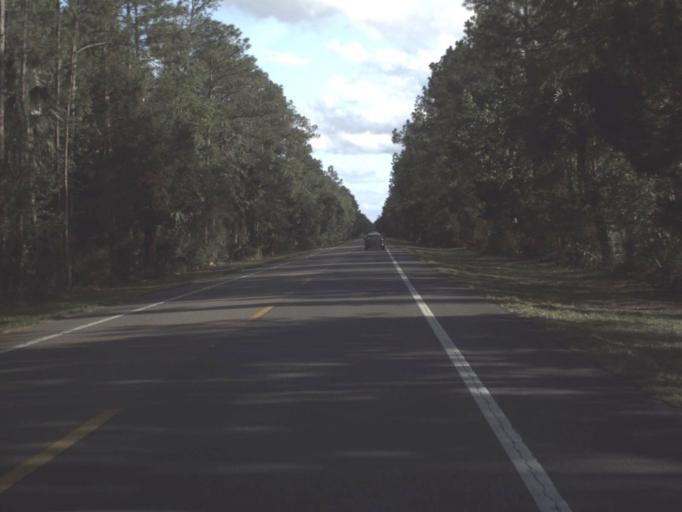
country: US
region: Florida
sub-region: Flagler County
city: Bunnell
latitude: 29.3679
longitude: -81.3118
